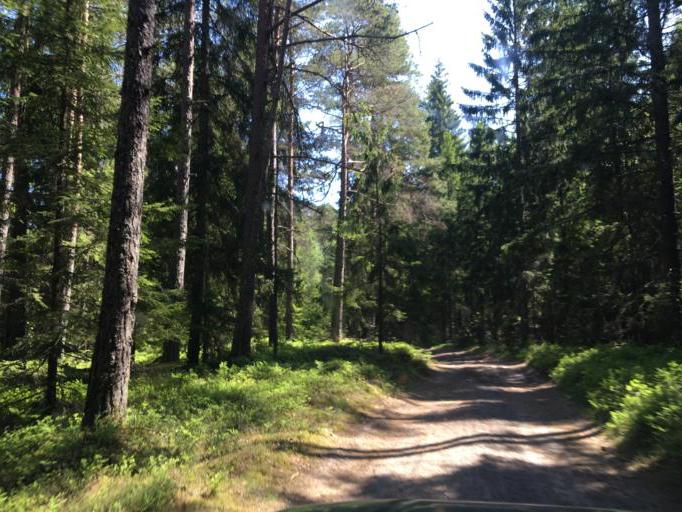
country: LV
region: Dundaga
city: Dundaga
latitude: 57.6032
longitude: 22.0948
